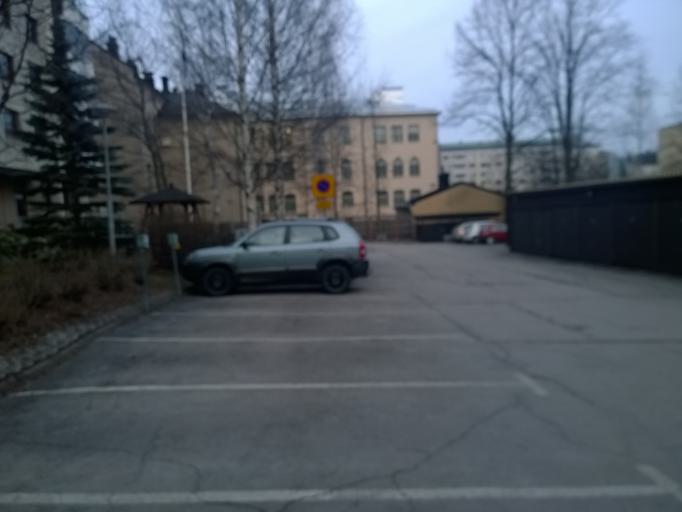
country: FI
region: Pirkanmaa
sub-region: Tampere
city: Tampere
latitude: 61.4942
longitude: 23.7506
